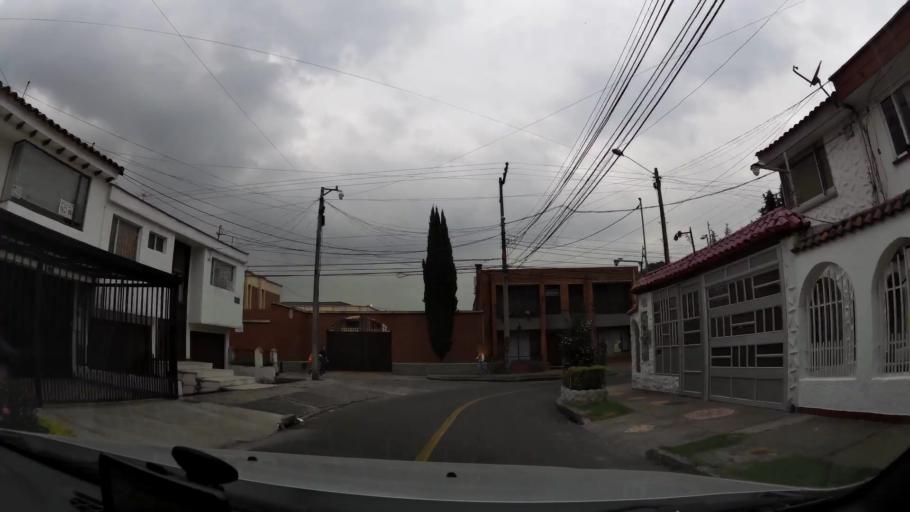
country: CO
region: Bogota D.C.
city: Bogota
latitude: 4.6684
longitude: -74.1204
